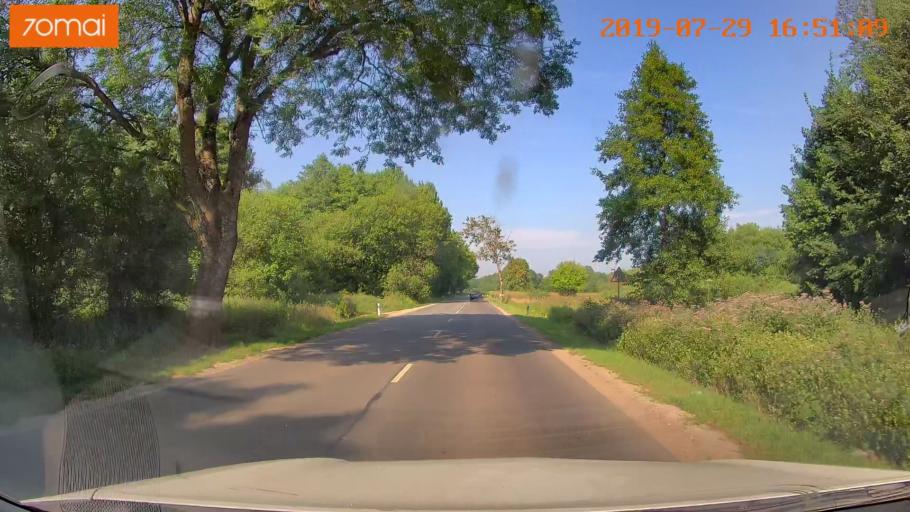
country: RU
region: Kaliningrad
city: Primorsk
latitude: 54.8071
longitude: 20.0638
